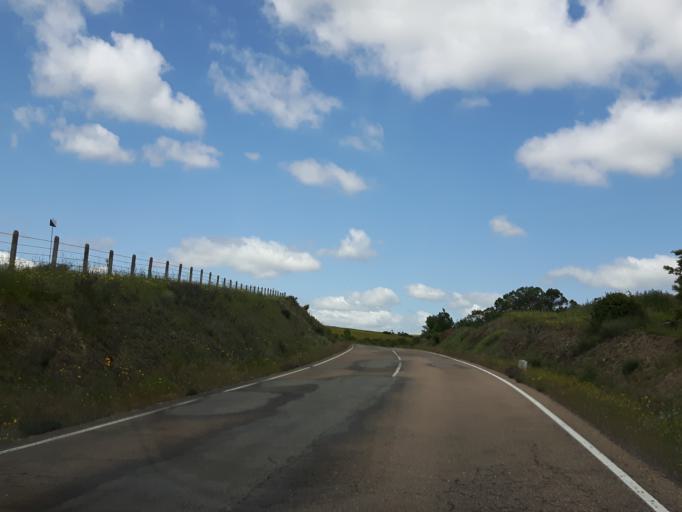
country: ES
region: Castille and Leon
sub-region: Provincia de Salamanca
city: Villar de la Yegua
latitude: 40.7154
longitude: -6.6890
